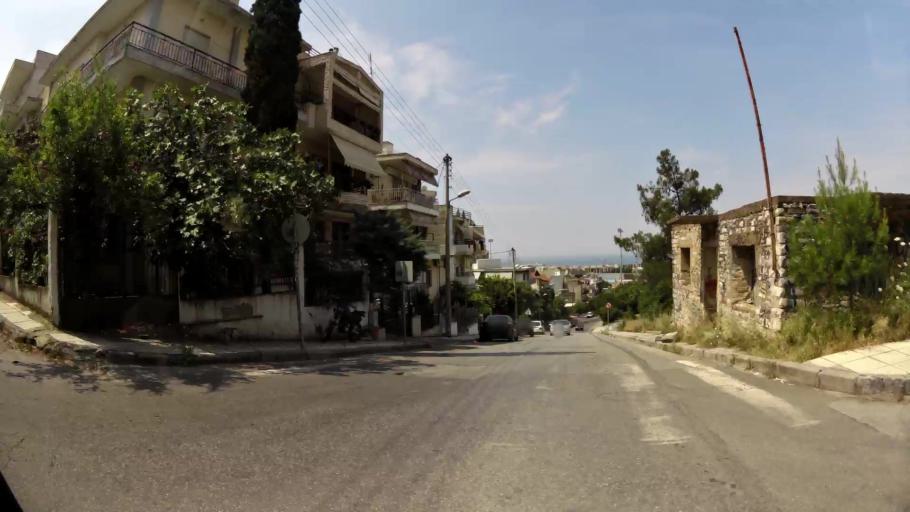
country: GR
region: Central Macedonia
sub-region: Nomos Thessalonikis
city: Agios Pavlos
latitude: 40.6291
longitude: 22.9685
